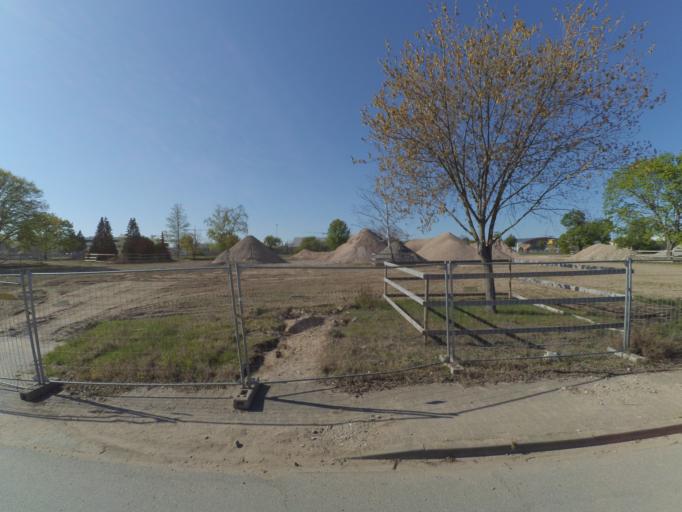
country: DE
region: Hesse
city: Viernheim
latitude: 49.5156
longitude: 8.5347
